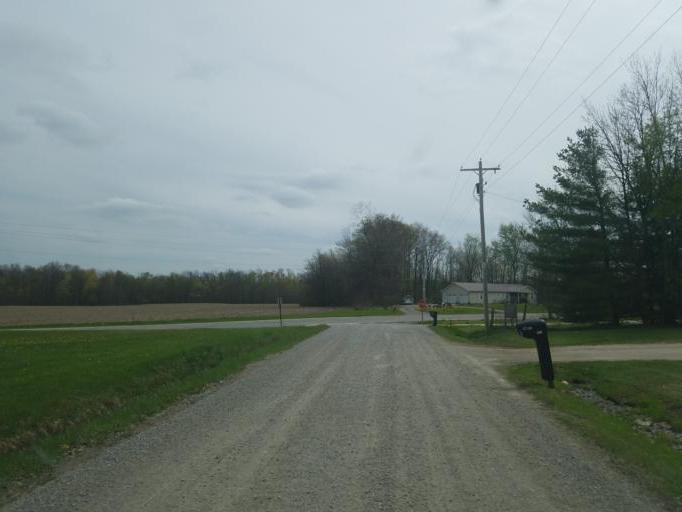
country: US
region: Ohio
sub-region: Morrow County
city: Mount Gilead
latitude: 40.5937
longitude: -82.7094
